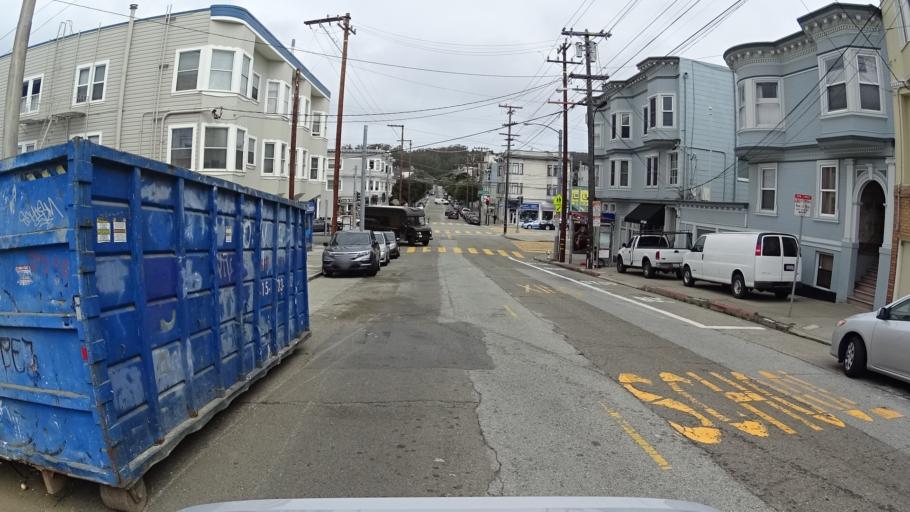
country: US
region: California
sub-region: San Francisco County
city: San Francisco
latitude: 37.7844
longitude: -122.4645
